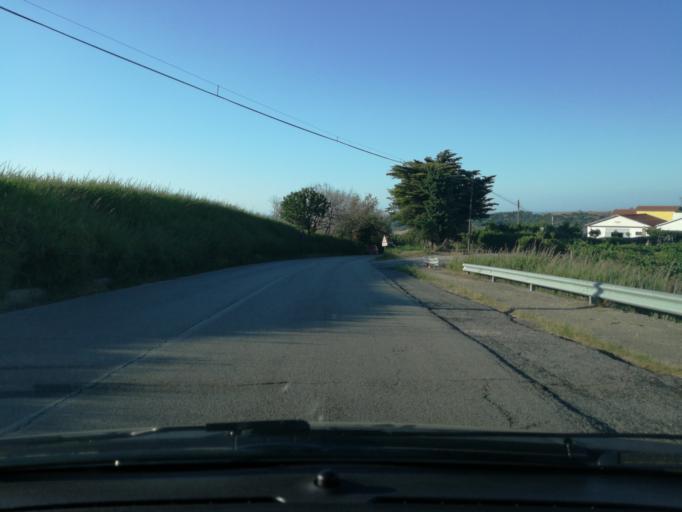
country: IT
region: Molise
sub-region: Provincia di Campobasso
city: Guglionesi
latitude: 41.9303
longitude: 14.9299
